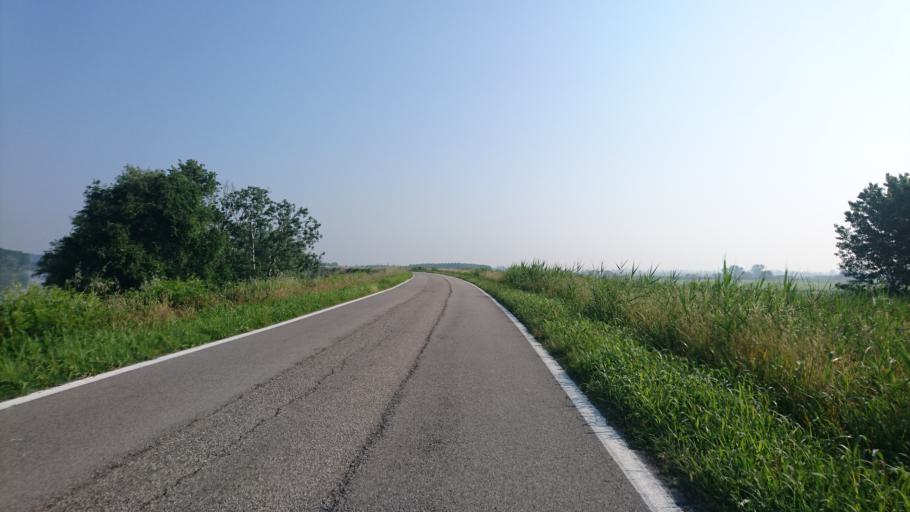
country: IT
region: Veneto
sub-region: Provincia di Rovigo
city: Castelnovo Bariano
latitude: 45.0408
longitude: 11.2713
